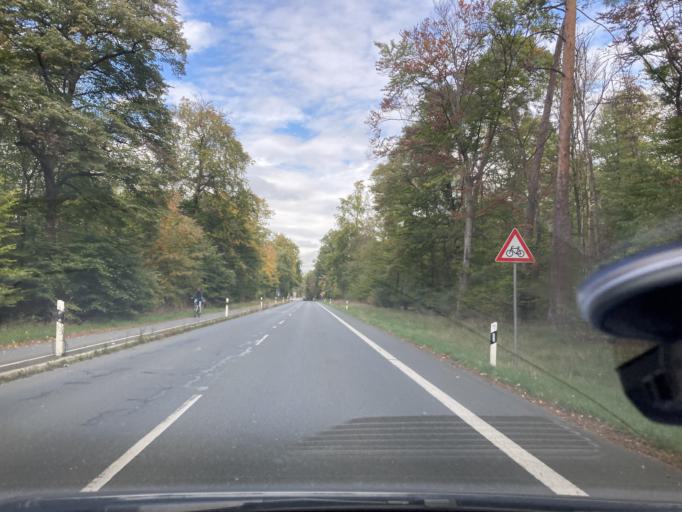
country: DE
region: Hesse
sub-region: Regierungsbezirk Darmstadt
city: Offenbach
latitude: 50.0725
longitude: 8.7651
